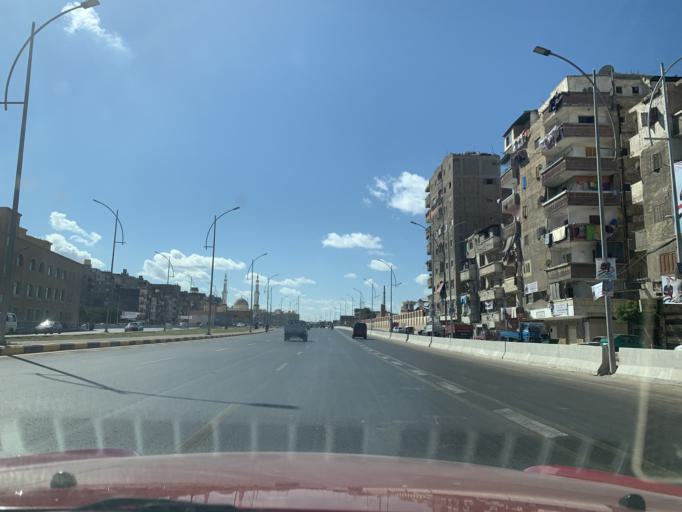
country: EG
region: Alexandria
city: Alexandria
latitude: 31.2226
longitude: 29.9702
